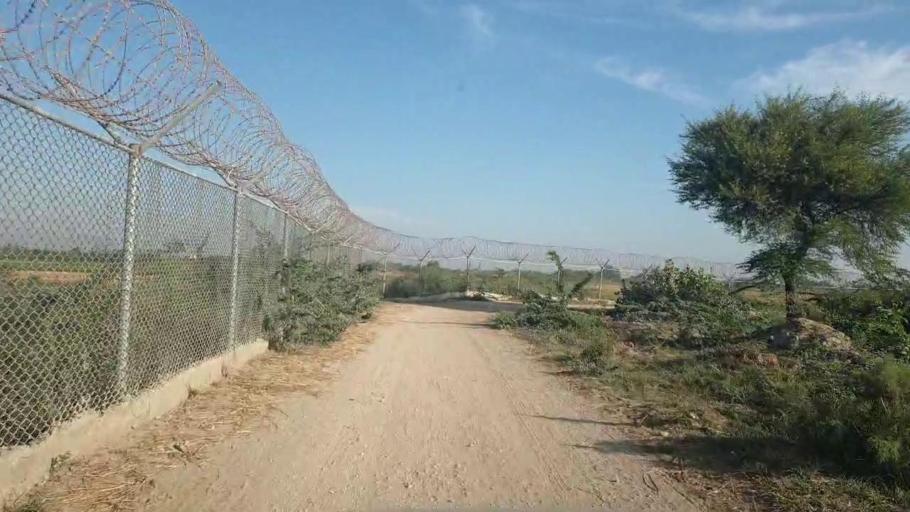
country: PK
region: Sindh
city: Talhar
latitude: 24.8486
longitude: 68.8570
